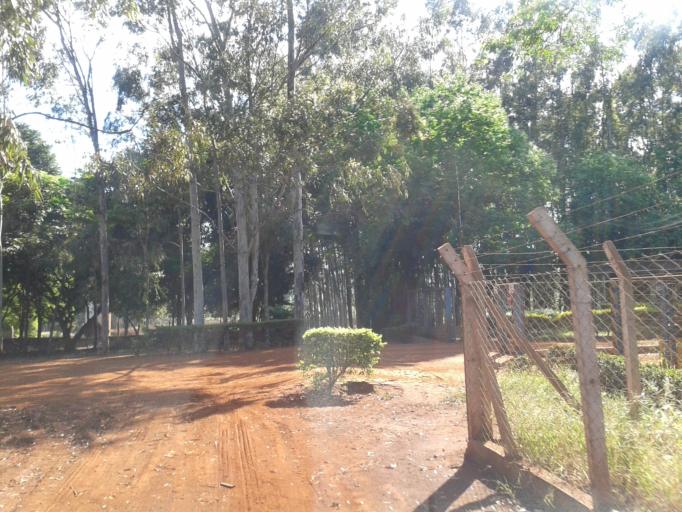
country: BR
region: Minas Gerais
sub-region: Centralina
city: Centralina
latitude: -18.6456
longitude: -49.2421
